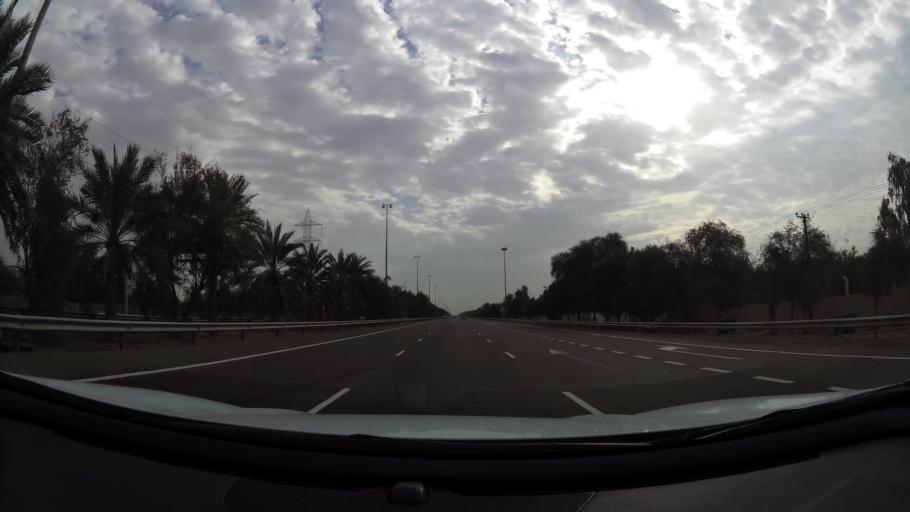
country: AE
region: Abu Dhabi
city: Al Ain
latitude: 24.2040
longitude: 55.4024
